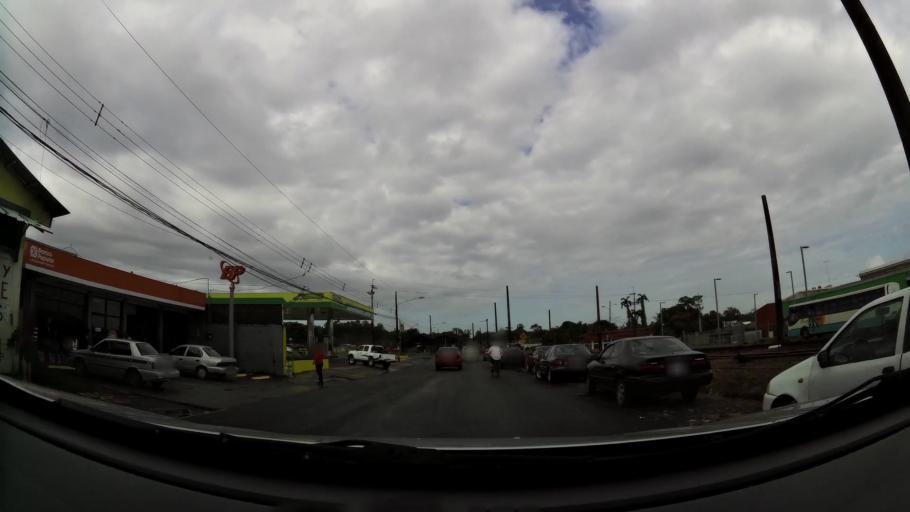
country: CR
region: Limon
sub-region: Canton de Siquirres
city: Siquirres
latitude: 10.0986
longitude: -83.5050
